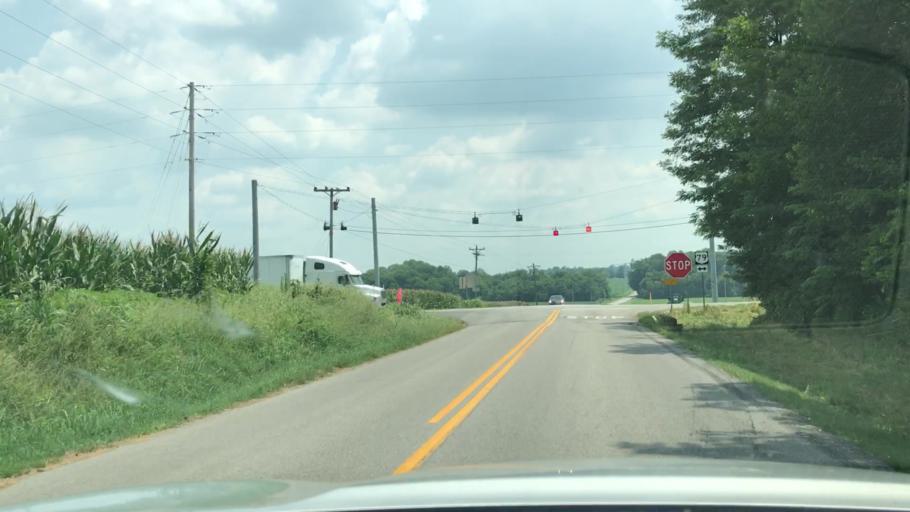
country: US
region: Kentucky
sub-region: Todd County
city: Elkton
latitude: 36.7254
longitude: -87.0872
